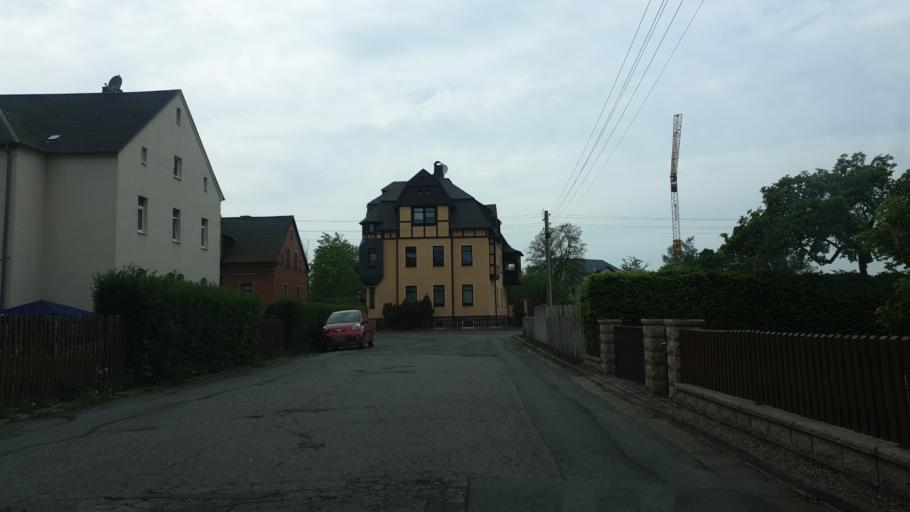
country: DE
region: Saxony
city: Lugau
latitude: 50.7385
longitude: 12.7478
